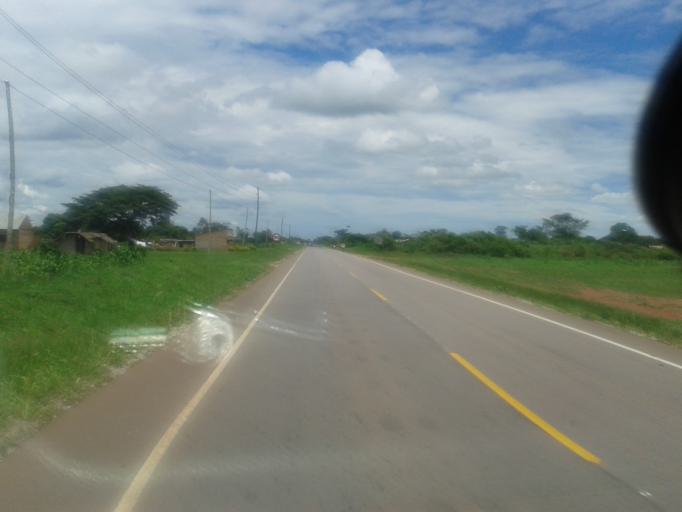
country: UG
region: Western Region
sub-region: Kiryandongo District
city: Masindi Port
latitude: 1.7723
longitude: 32.0188
